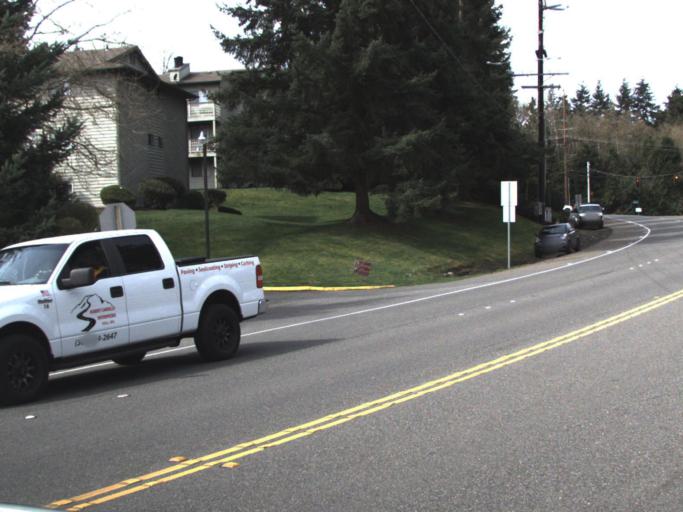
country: US
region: Washington
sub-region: King County
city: Normandy Park
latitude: 47.4473
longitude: -122.3320
